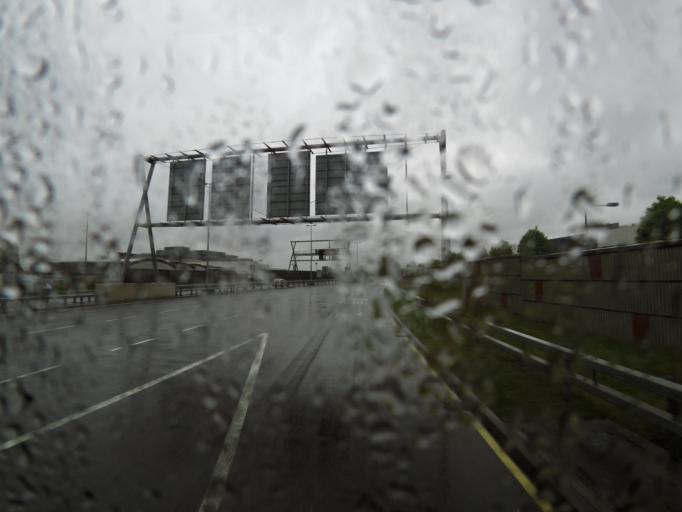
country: IE
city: Fairview
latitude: 53.3568
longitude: -6.2291
